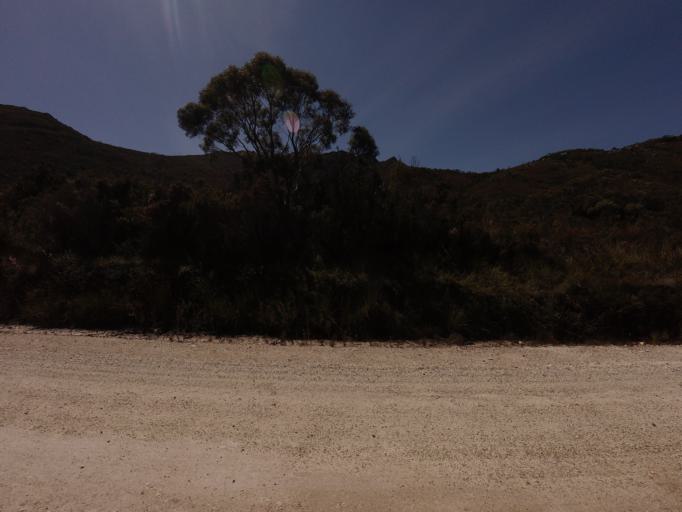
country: AU
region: Tasmania
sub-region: Huon Valley
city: Geeveston
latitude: -42.9372
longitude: 146.3477
